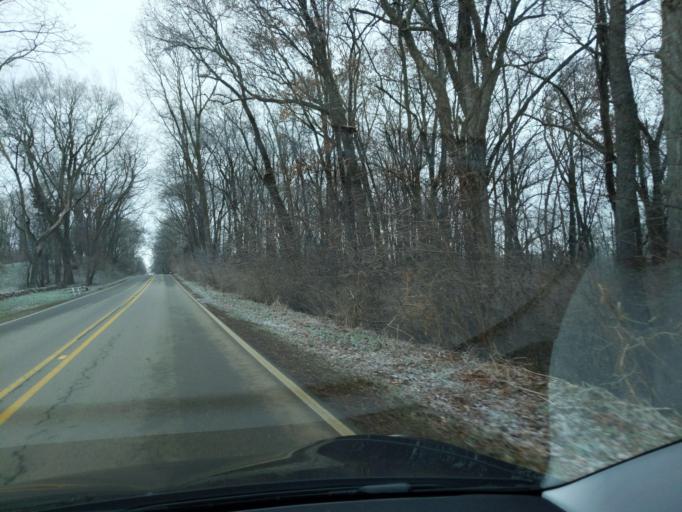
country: US
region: Michigan
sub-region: Jackson County
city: Spring Arbor
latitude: 42.1978
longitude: -84.5402
